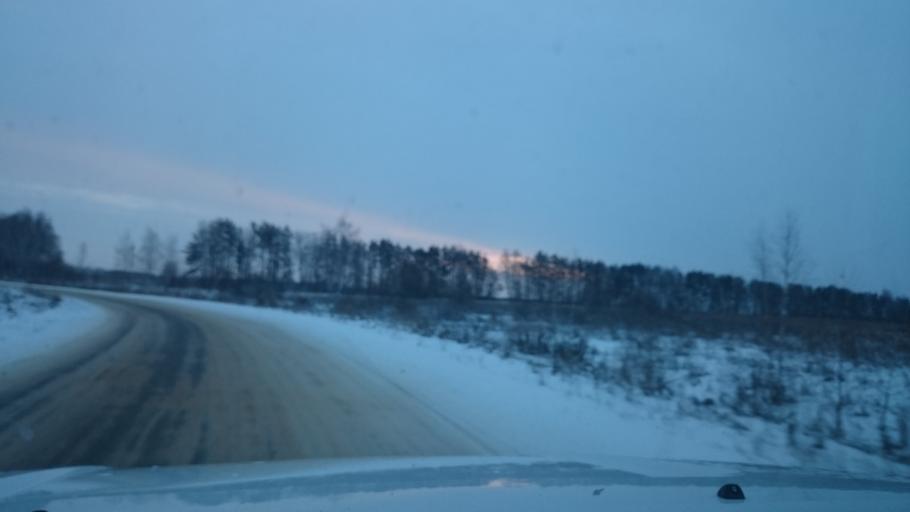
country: RU
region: Tula
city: Leninskiy
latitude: 54.2415
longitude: 37.2887
